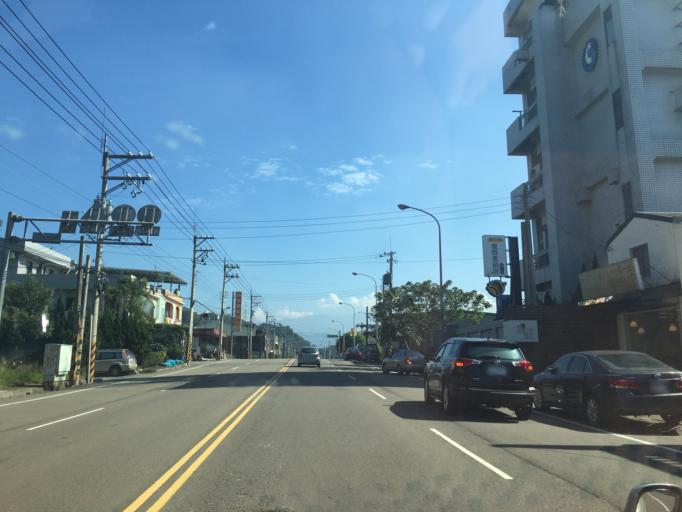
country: TW
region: Taiwan
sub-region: Hsinchu
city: Zhubei
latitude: 24.8117
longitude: 121.1324
